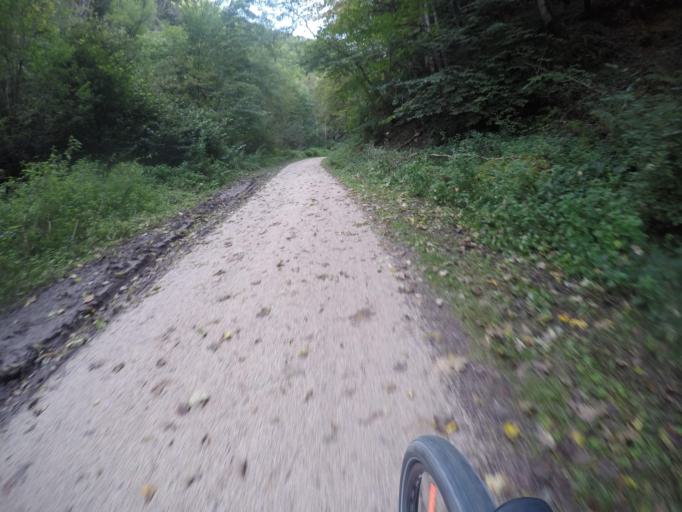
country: DE
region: Baden-Wuerttemberg
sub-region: Tuebingen Region
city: Munsingen
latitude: 48.4420
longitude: 9.4671
